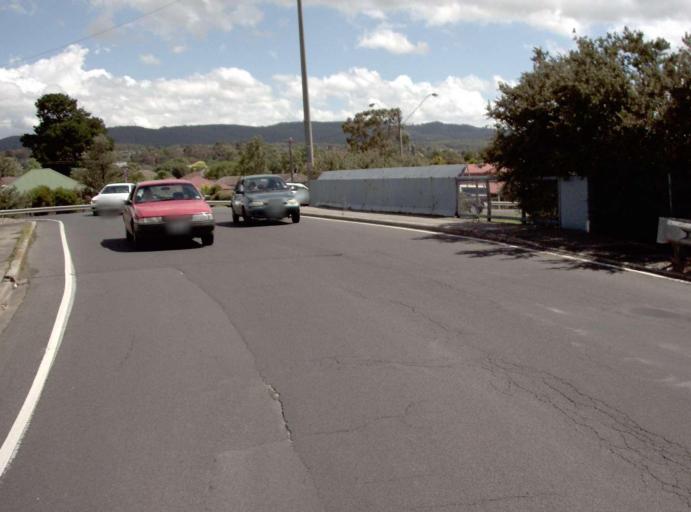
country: AU
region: Victoria
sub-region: Latrobe
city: Moe
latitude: -38.1768
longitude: 146.2648
